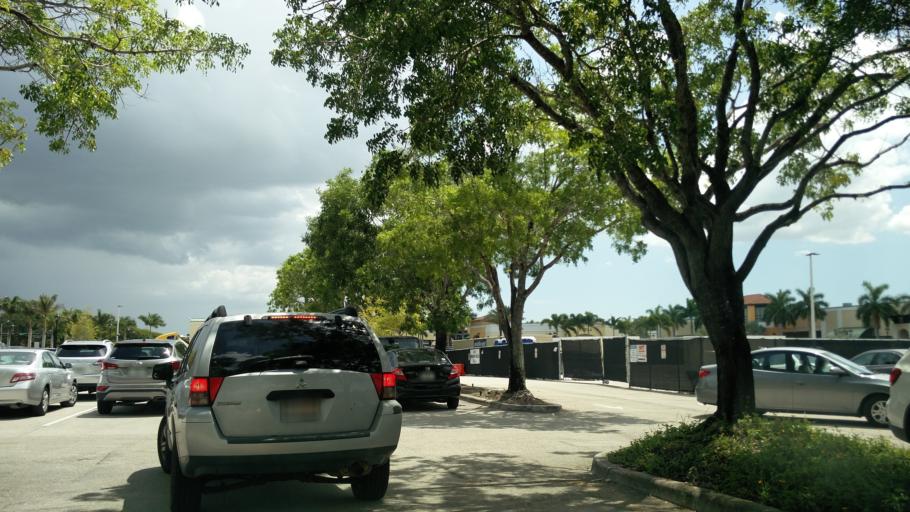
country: US
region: Florida
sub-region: Broward County
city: Pine Island Ridge
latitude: 26.1500
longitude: -80.3186
